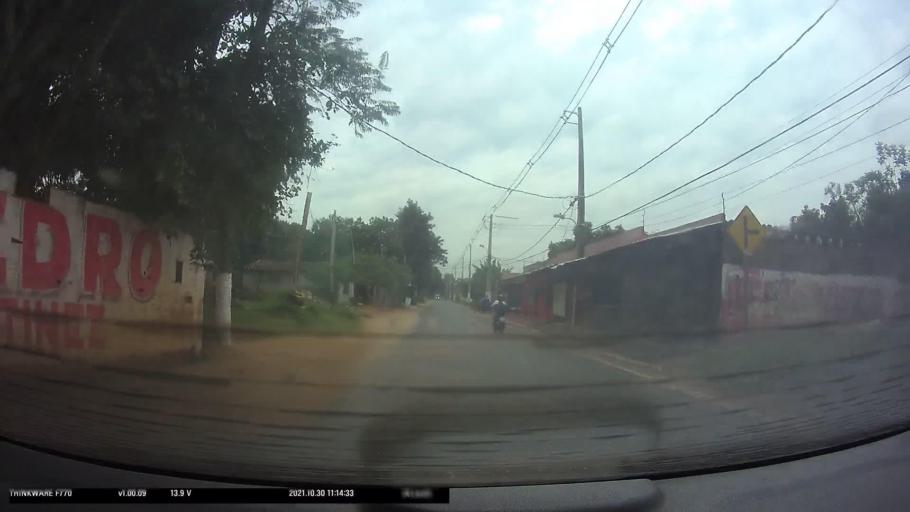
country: PY
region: Central
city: San Lorenzo
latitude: -25.3118
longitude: -57.5120
